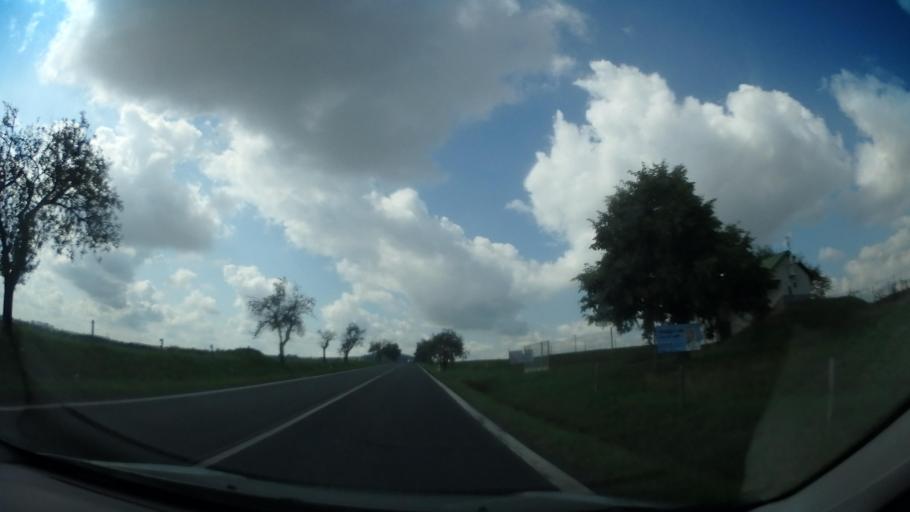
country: CZ
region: Central Bohemia
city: Cervene Pecky
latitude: 49.9484
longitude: 15.2219
